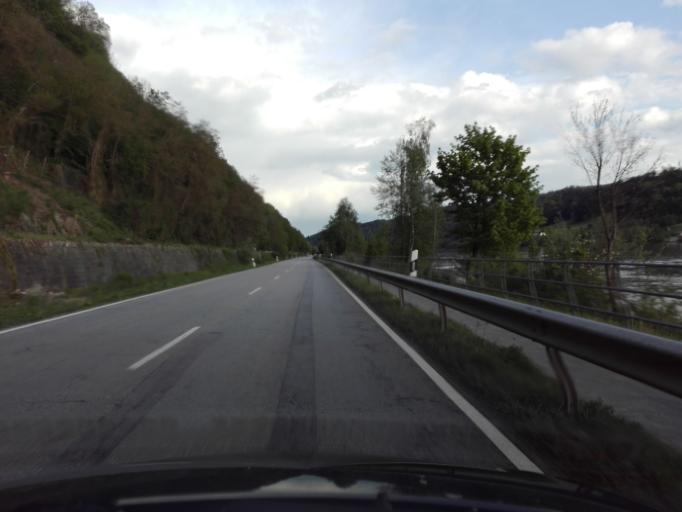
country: DE
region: Bavaria
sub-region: Lower Bavaria
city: Obernzell
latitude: 48.5664
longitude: 13.6077
